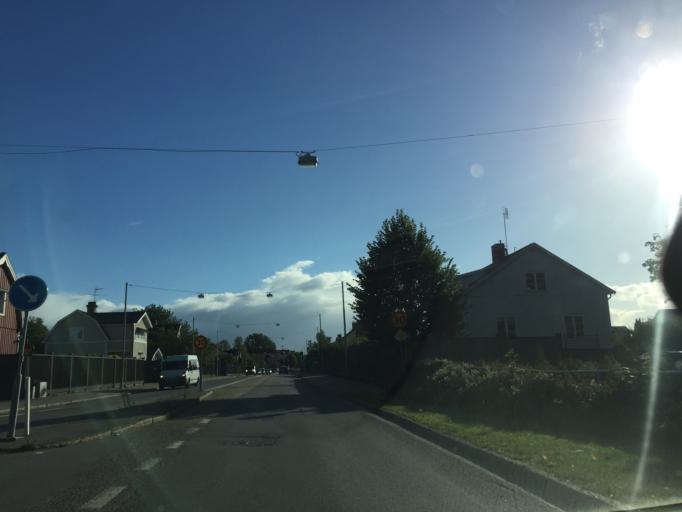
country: SE
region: OErebro
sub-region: Orebro Kommun
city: Orebro
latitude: 59.2874
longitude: 15.2042
